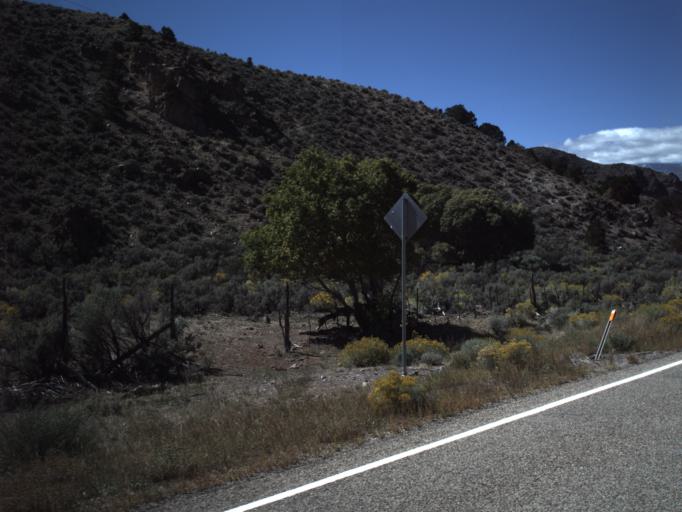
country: US
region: Utah
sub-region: Piute County
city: Junction
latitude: 38.2028
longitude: -112.1578
